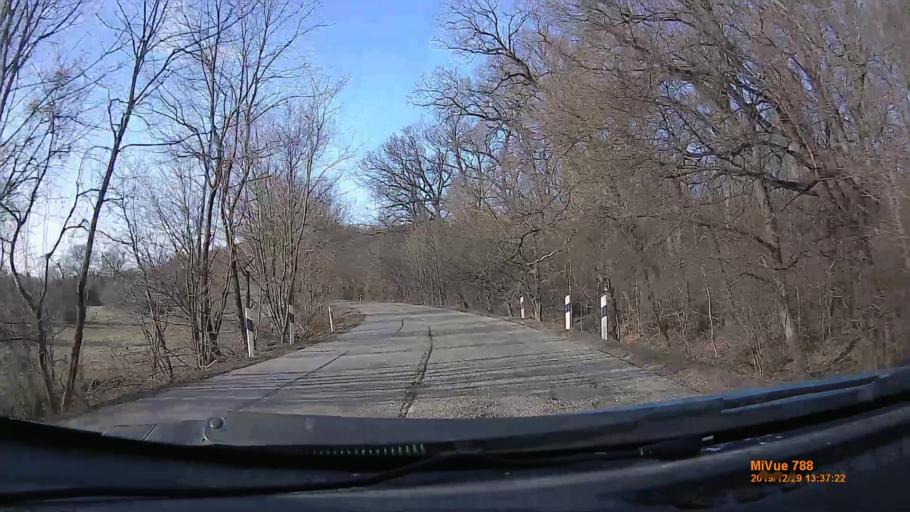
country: HU
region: Heves
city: Sirok
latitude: 47.9229
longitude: 20.1697
